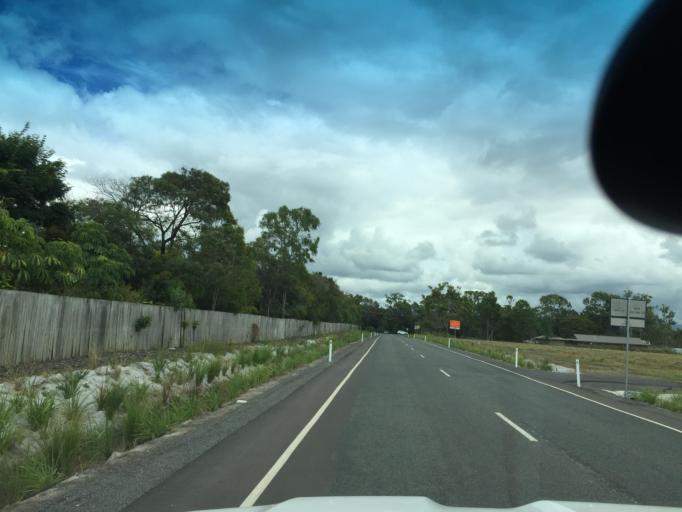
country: AU
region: Queensland
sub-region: Moreton Bay
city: Burpengary
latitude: -27.1650
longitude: 152.9830
